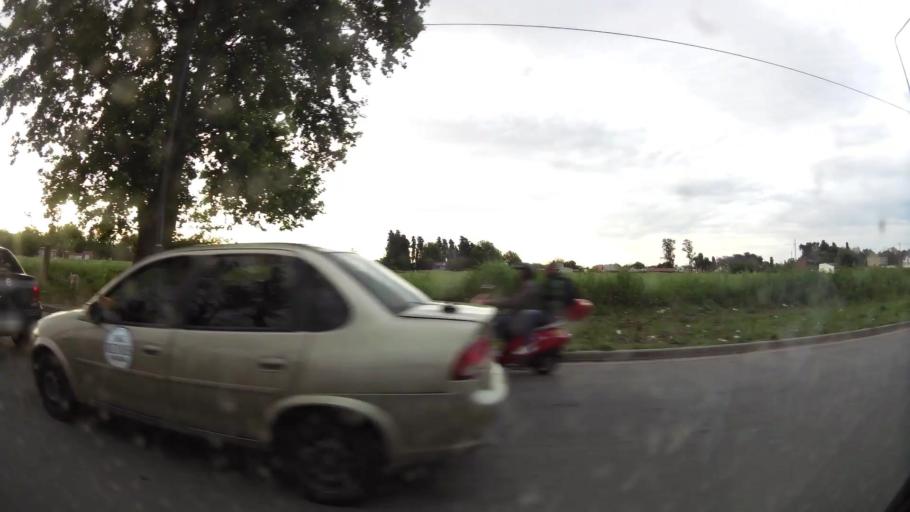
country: AR
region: Buenos Aires
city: San Nicolas de los Arroyos
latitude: -33.3555
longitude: -60.2022
